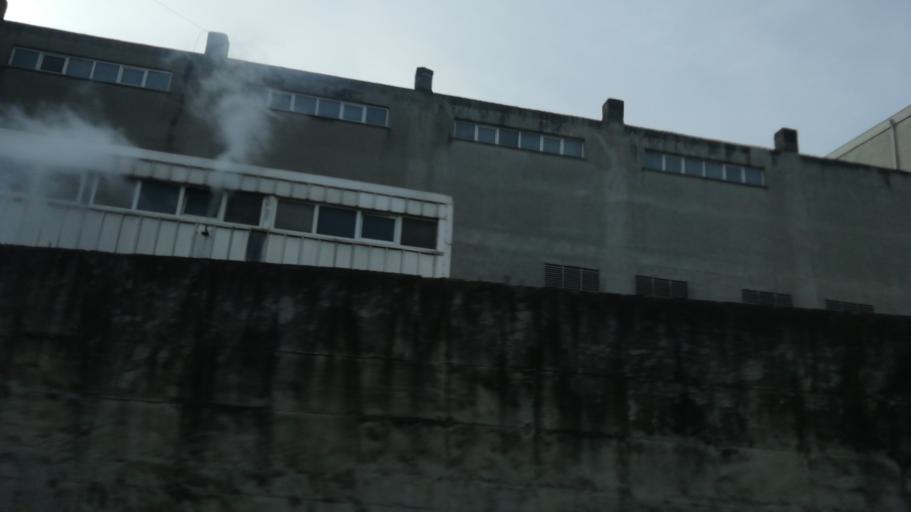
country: TR
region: Istanbul
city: Basaksehir
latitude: 41.0778
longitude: 28.8125
